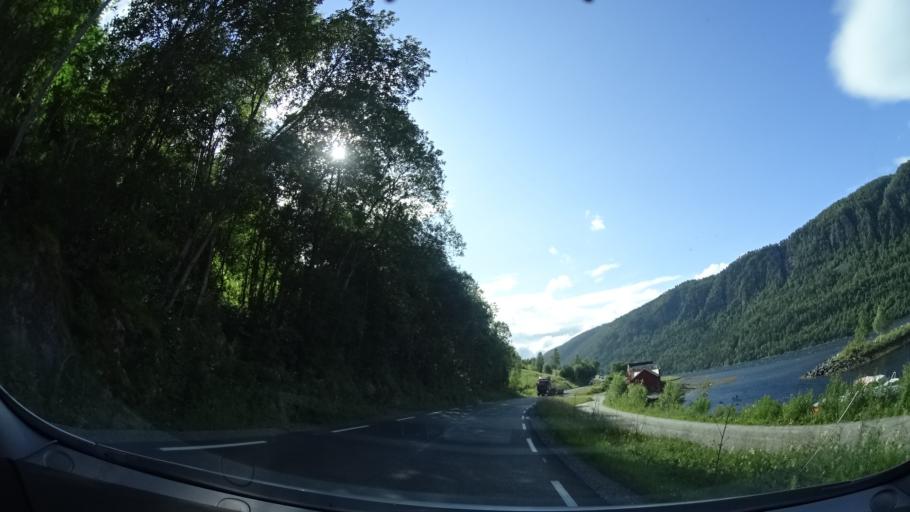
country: NO
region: Sor-Trondelag
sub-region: Hemne
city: Kyrksaeterora
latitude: 63.1996
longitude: 8.9779
